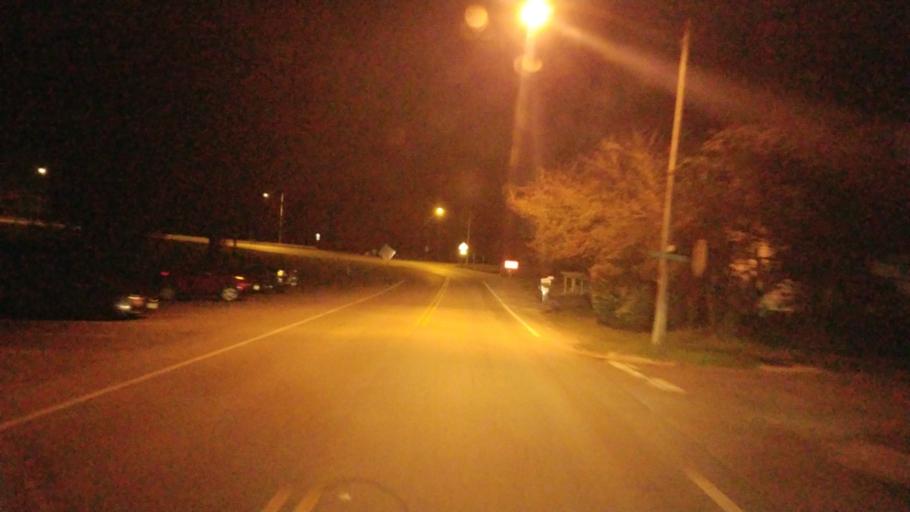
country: US
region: Ohio
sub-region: Hocking County
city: Logan
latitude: 39.5333
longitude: -82.4092
